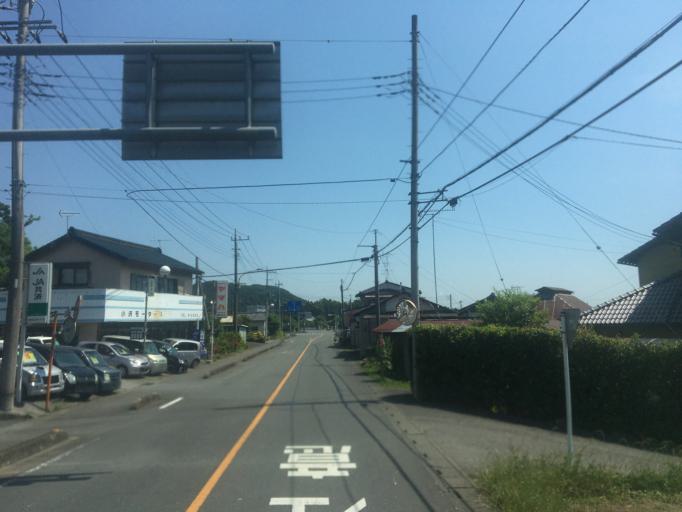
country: JP
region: Saitama
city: Ogawa
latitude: 36.0106
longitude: 139.2953
